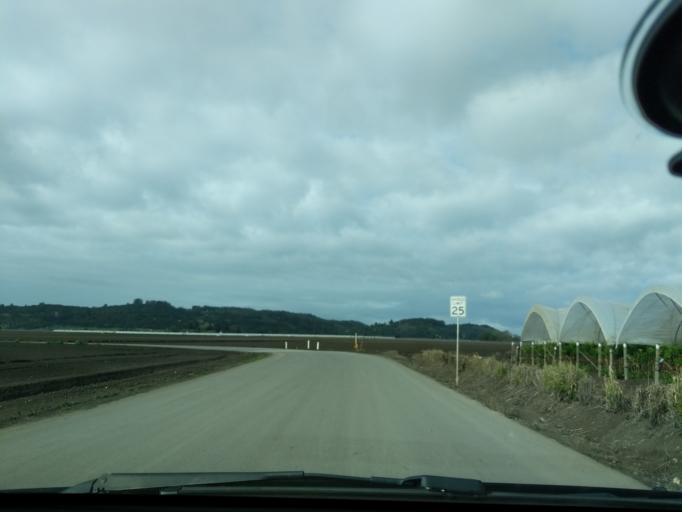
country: US
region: California
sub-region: San Benito County
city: Aromas
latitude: 36.9035
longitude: -121.6701
